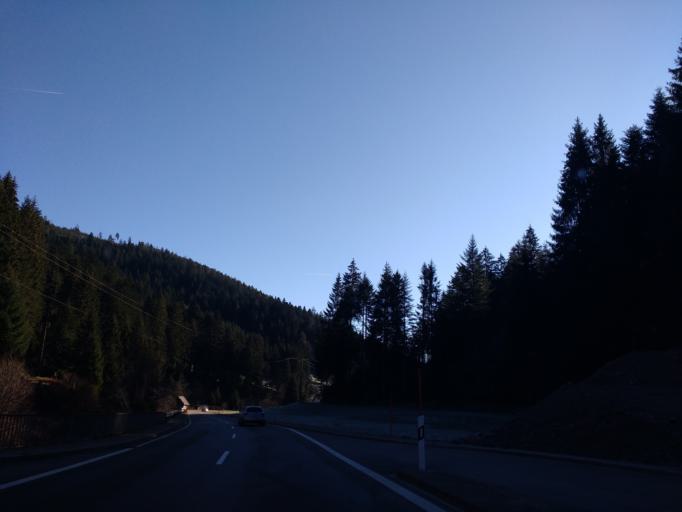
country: DE
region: Baden-Wuerttemberg
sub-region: Karlsruhe Region
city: Bad Rippoldsau-Schapbach
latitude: 48.4441
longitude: 8.3110
